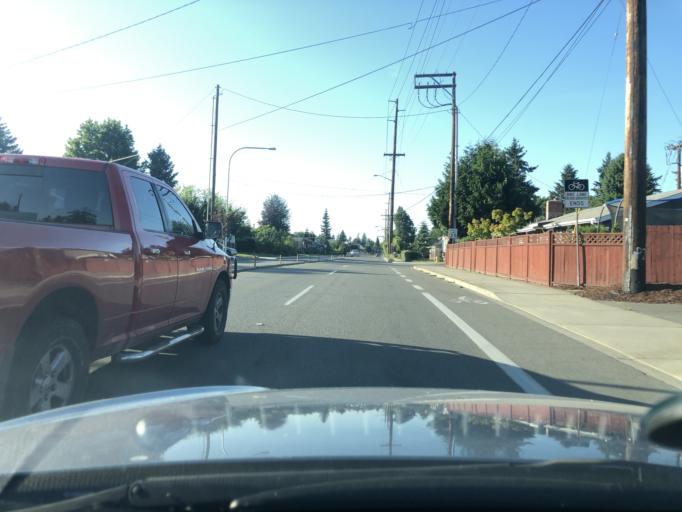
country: US
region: Washington
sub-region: King County
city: Auburn
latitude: 47.3049
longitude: -122.2133
